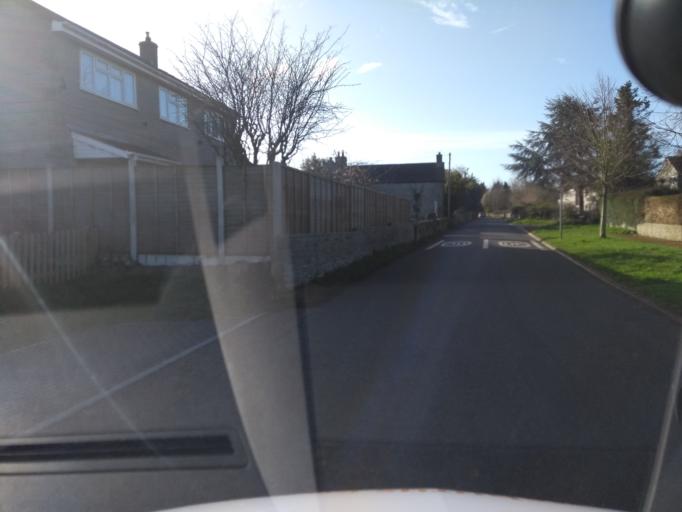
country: GB
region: England
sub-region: Somerset
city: Wedmore
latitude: 51.1401
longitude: -2.8330
